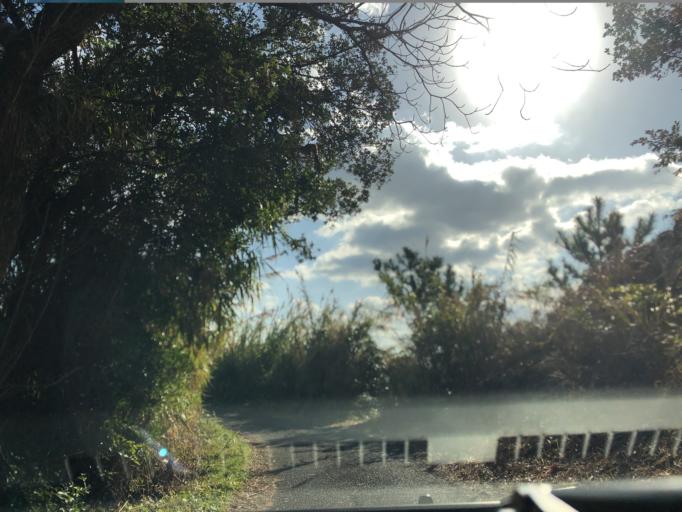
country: JP
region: Kochi
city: Sukumo
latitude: 32.9105
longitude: 132.6953
